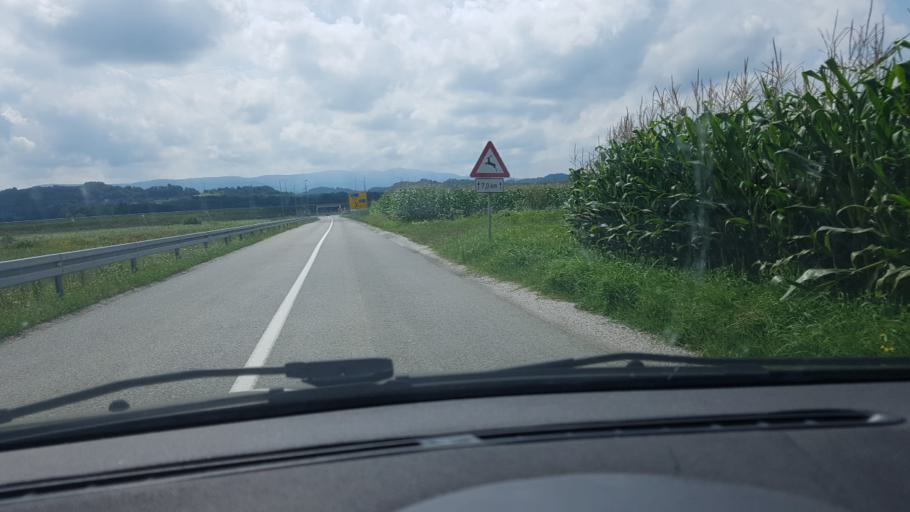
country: HR
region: Krapinsko-Zagorska
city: Bedekovcina
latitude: 46.0363
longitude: 15.9948
